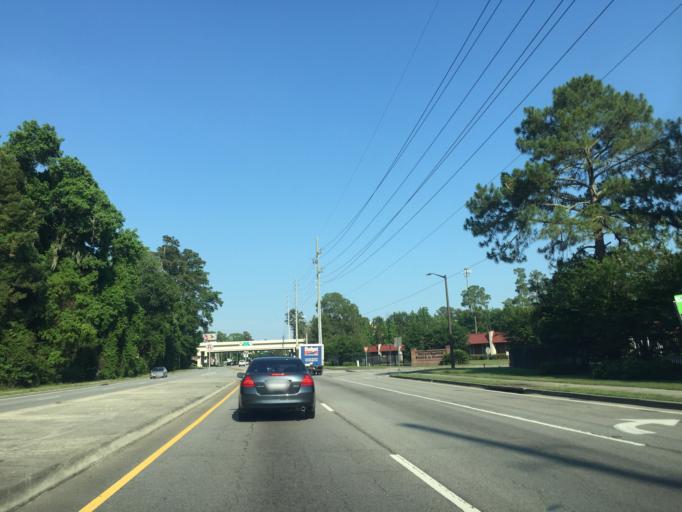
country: US
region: Georgia
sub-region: Chatham County
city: Isle of Hope
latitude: 32.0013
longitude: -81.0818
